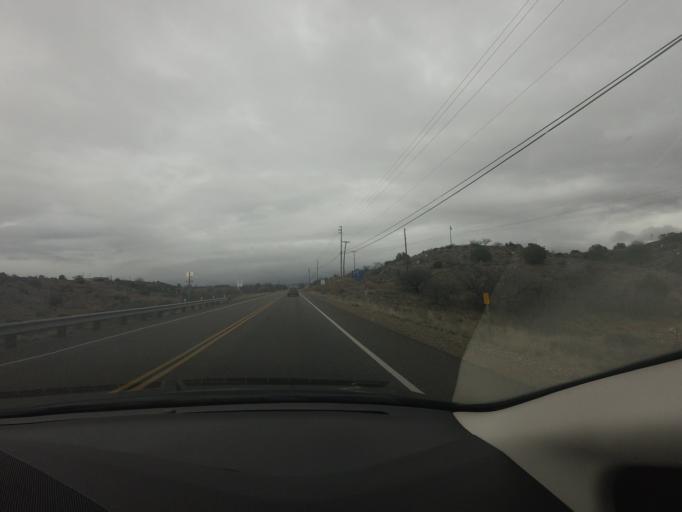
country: US
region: Arizona
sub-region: Yavapai County
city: Lake Montezuma
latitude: 34.6401
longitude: -111.7998
